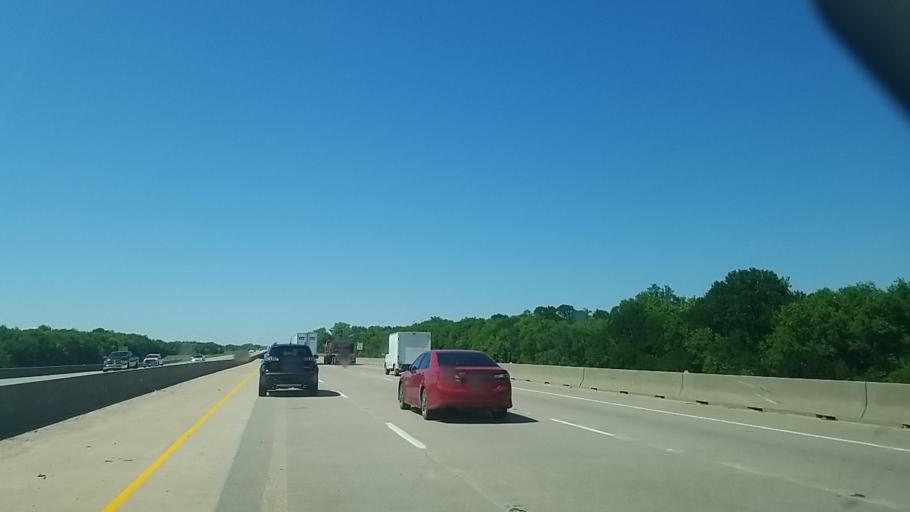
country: US
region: Texas
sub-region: Navarro County
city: Corsicana
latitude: 32.1573
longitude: -96.4684
